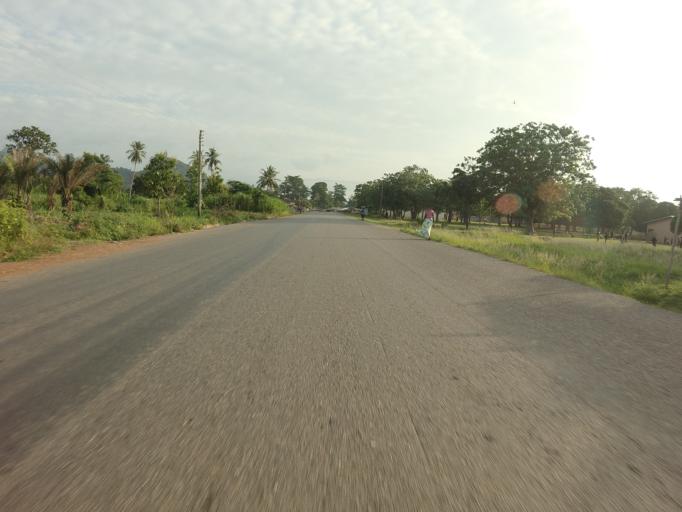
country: GH
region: Volta
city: Kpandu
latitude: 6.9012
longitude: 0.4354
